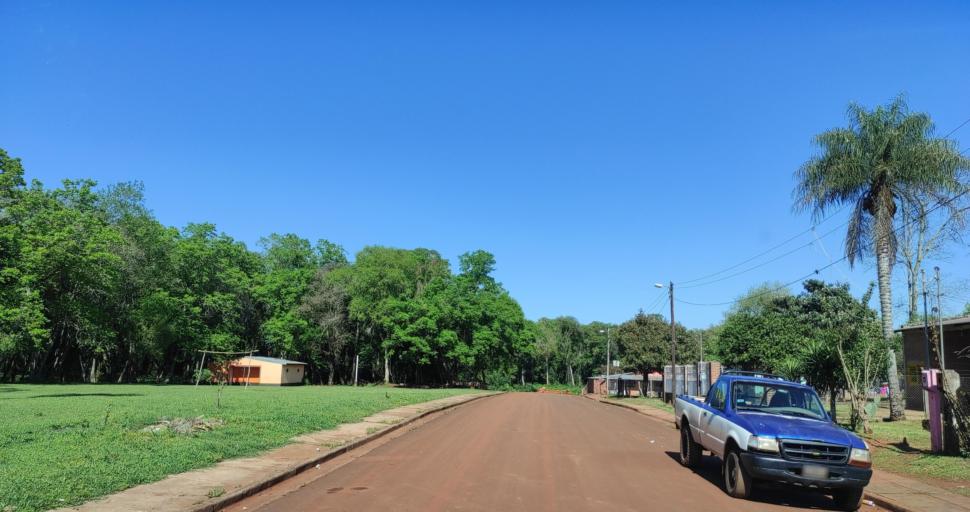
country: AR
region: Misiones
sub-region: Departamento de Candelaria
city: Loreto
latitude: -27.3328
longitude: -55.5233
